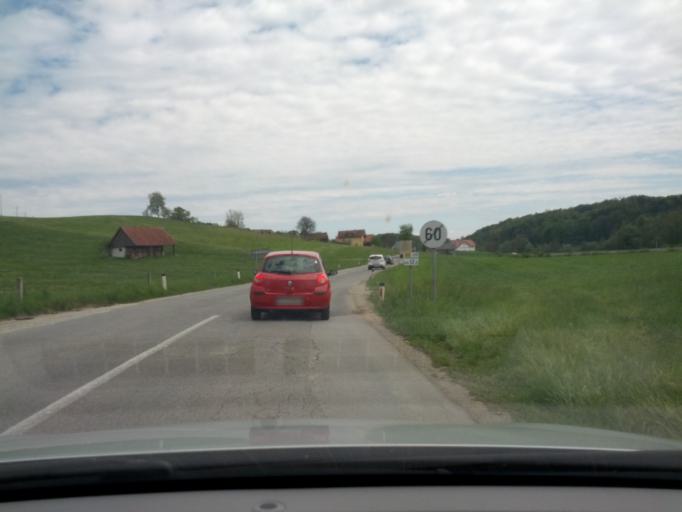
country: SI
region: Smarje pri Jelsah
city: Smarje pri Jelsah
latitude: 46.2340
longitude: 15.5354
